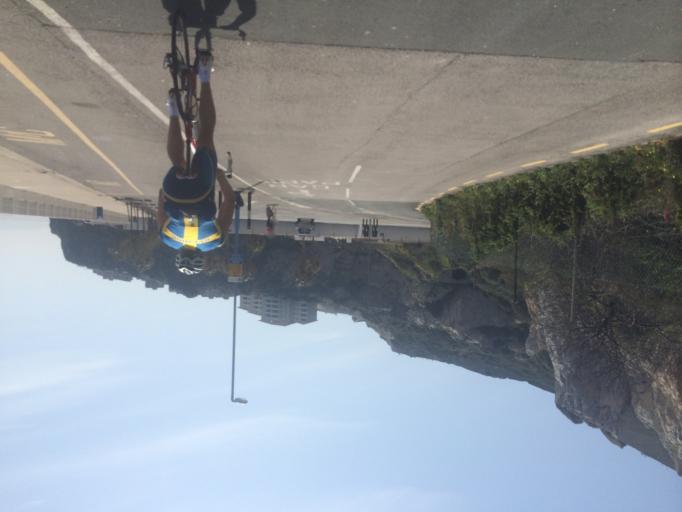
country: GI
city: Gibraltar
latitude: 36.1174
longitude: -5.3504
